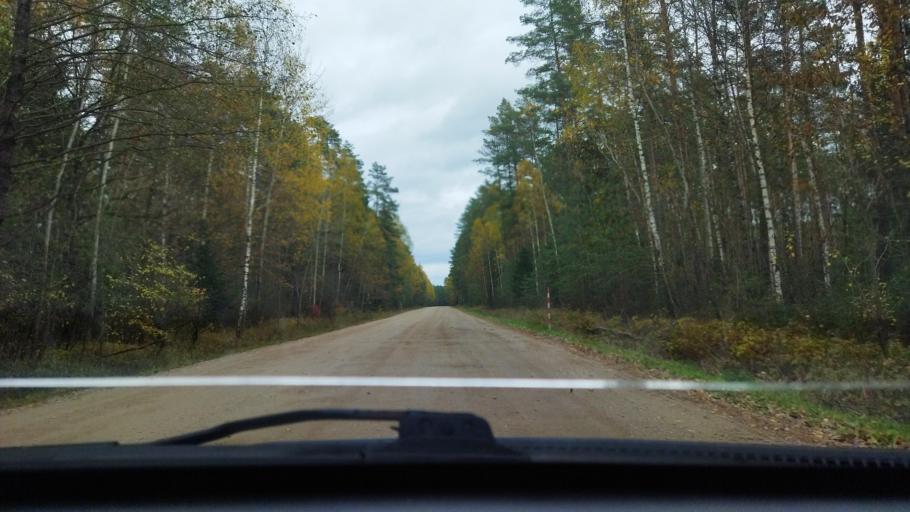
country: BY
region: Minsk
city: Svir
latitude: 54.8038
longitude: 26.2477
